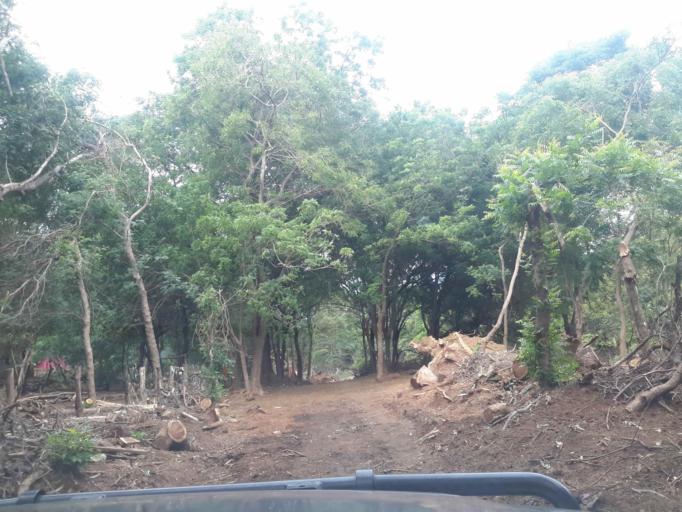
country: NI
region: Carazo
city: Santa Teresa
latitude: 11.6819
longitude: -86.3001
